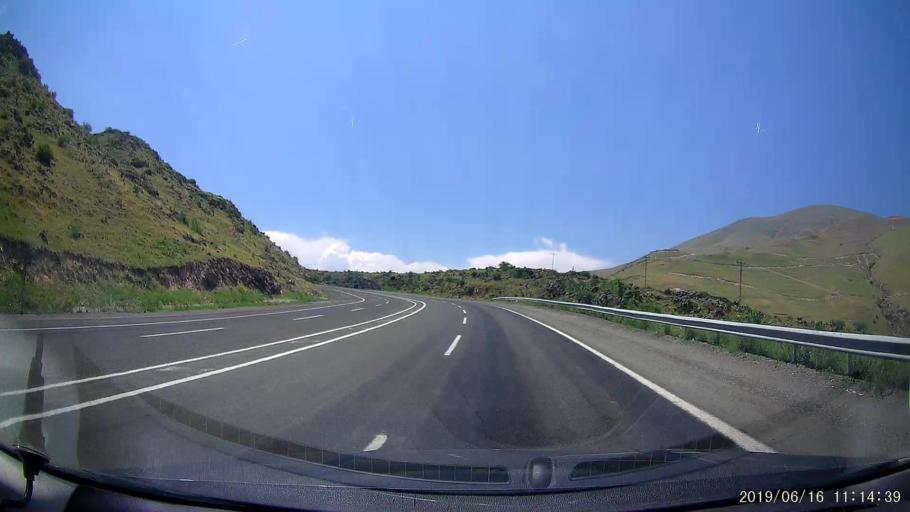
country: TR
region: Igdir
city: Igdir
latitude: 39.7755
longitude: 44.1416
